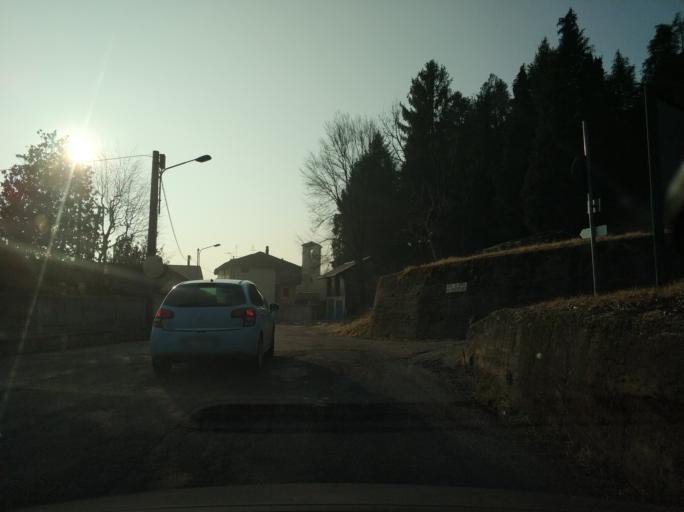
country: IT
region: Piedmont
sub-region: Provincia di Torino
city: Front
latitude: 45.2820
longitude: 7.6618
